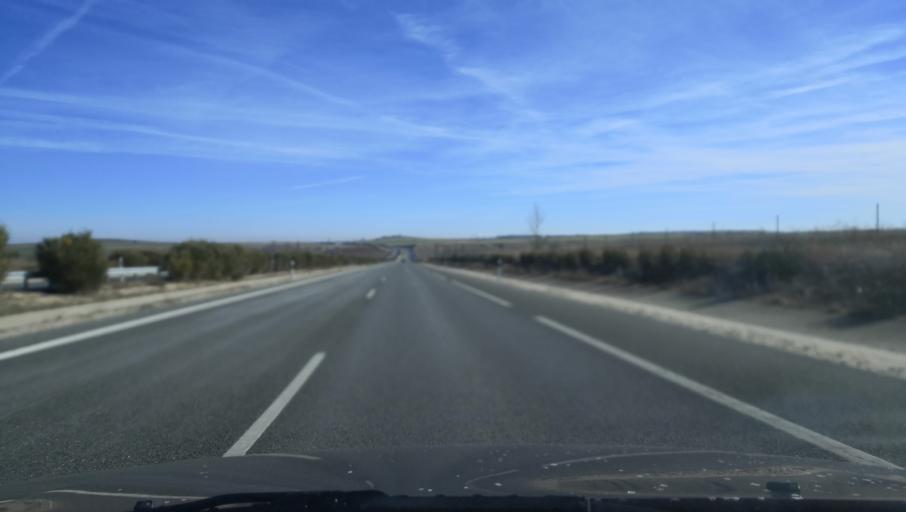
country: ES
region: Castille and Leon
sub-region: Provincia de Avila
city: Salvadios
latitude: 40.8726
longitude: -5.0841
